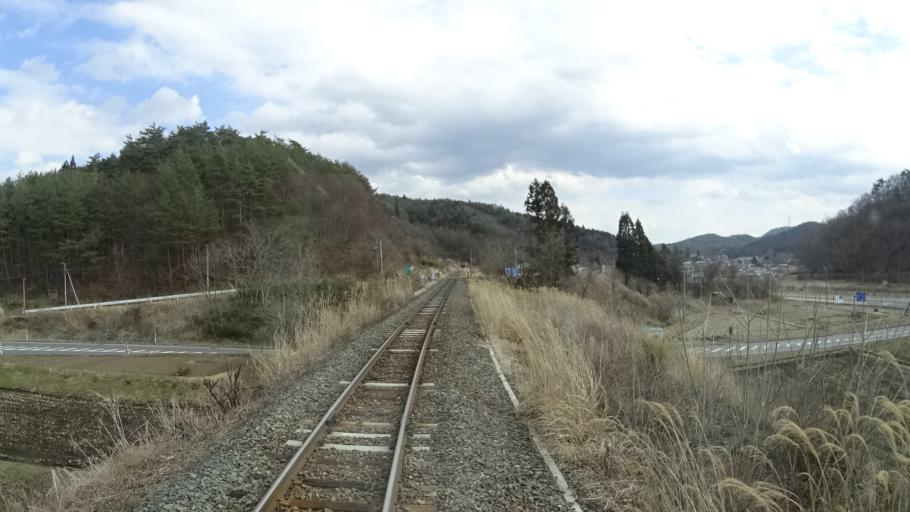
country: JP
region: Iwate
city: Tono
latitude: 39.3543
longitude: 141.3469
